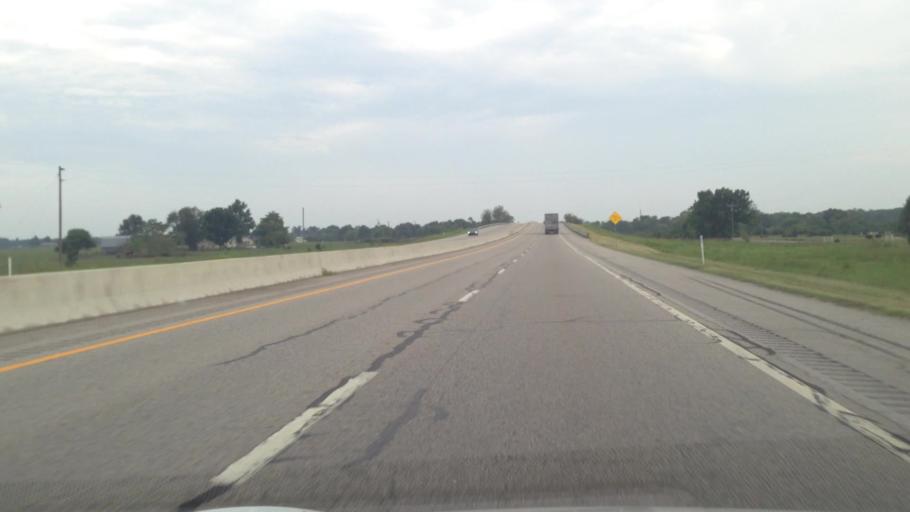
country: US
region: Oklahoma
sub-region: Ottawa County
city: Miami
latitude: 36.8191
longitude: -94.8719
